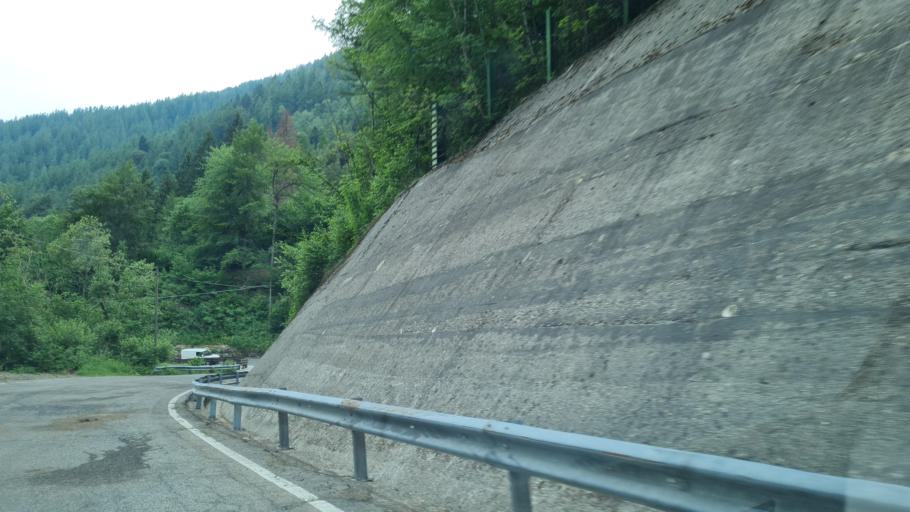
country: IT
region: Piedmont
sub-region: Provincia di Torino
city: Valprato Soana
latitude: 45.5339
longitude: 7.5404
